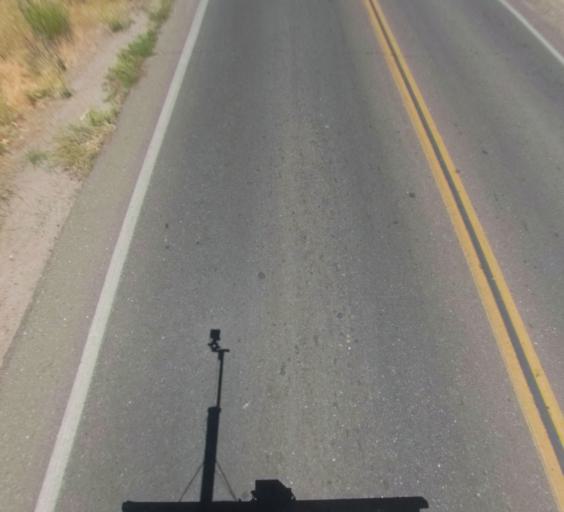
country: US
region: California
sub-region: Madera County
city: Parksdale
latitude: 36.9596
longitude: -120.0196
